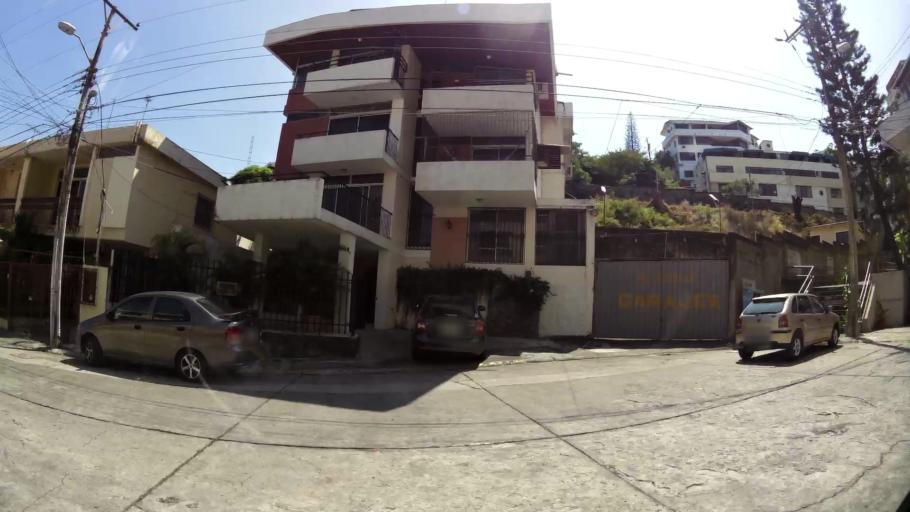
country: EC
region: Guayas
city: Guayaquil
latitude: -2.1646
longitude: -79.9080
